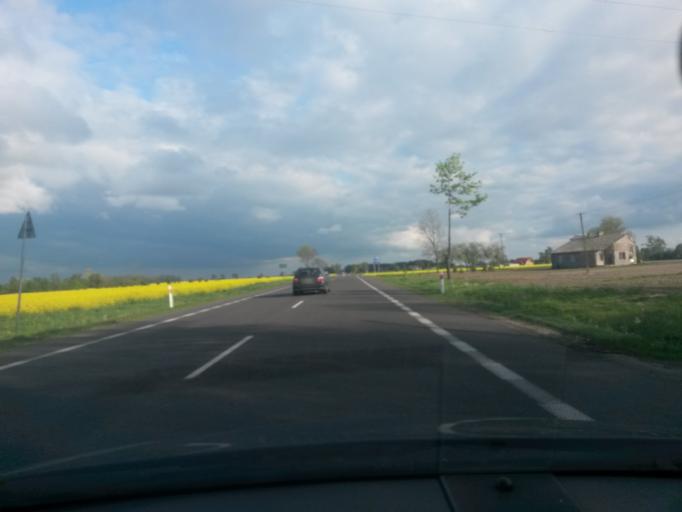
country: PL
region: Masovian Voivodeship
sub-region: Powiat plocki
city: Drobin
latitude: 52.7177
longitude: 20.0206
